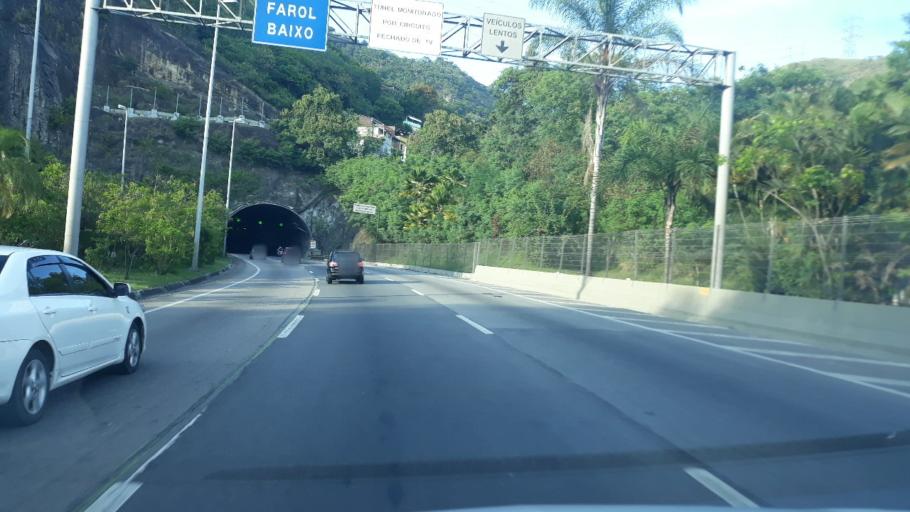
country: BR
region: Rio de Janeiro
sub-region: Rio De Janeiro
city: Rio de Janeiro
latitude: -22.9079
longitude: -43.3145
